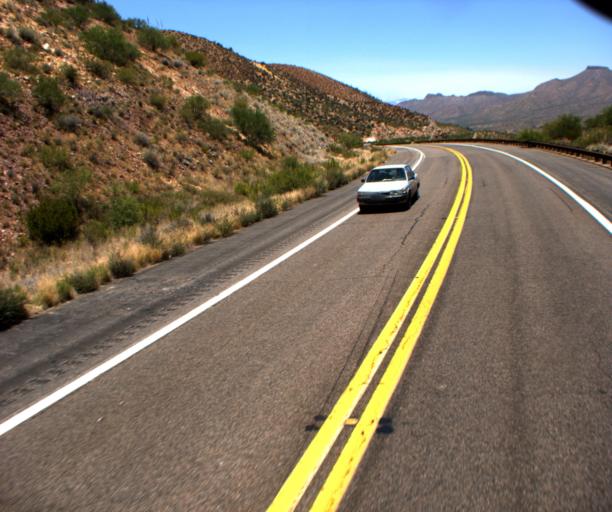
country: US
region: Arizona
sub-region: Gila County
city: Claypool
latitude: 33.5053
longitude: -110.8679
